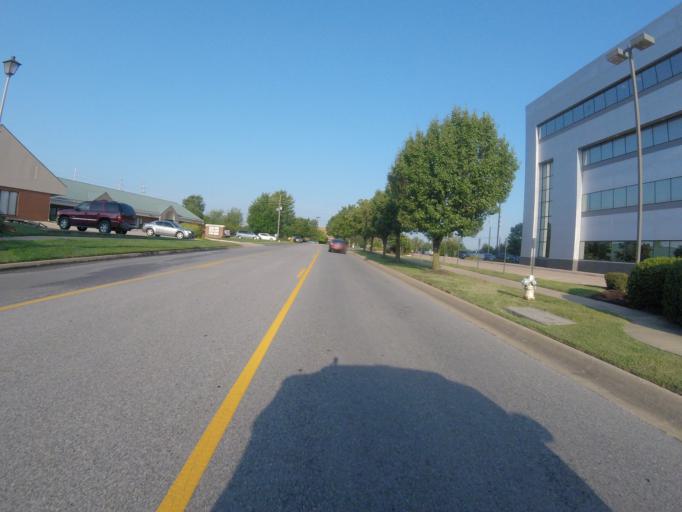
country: US
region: Arkansas
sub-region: Washington County
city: Johnson
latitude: 36.1139
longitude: -94.1530
